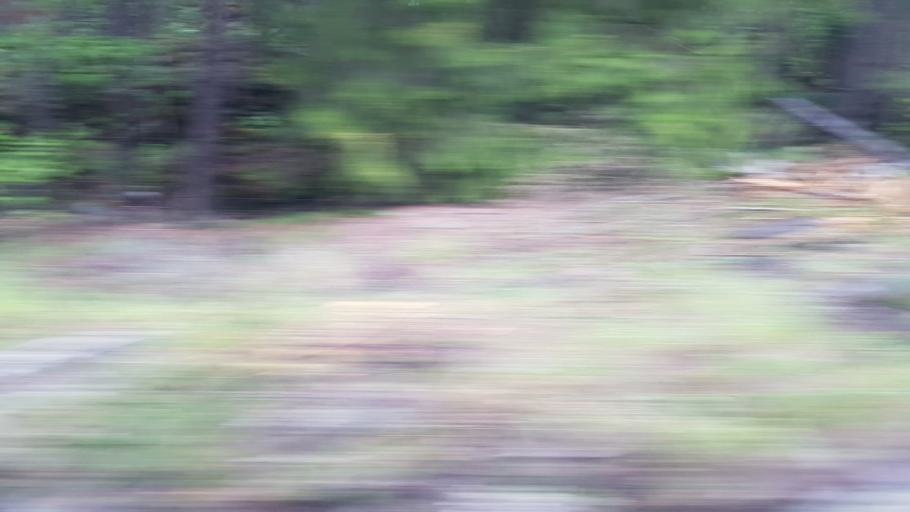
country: NO
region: Oppland
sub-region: Sor-Fron
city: Hundorp
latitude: 61.5708
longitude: 9.8611
